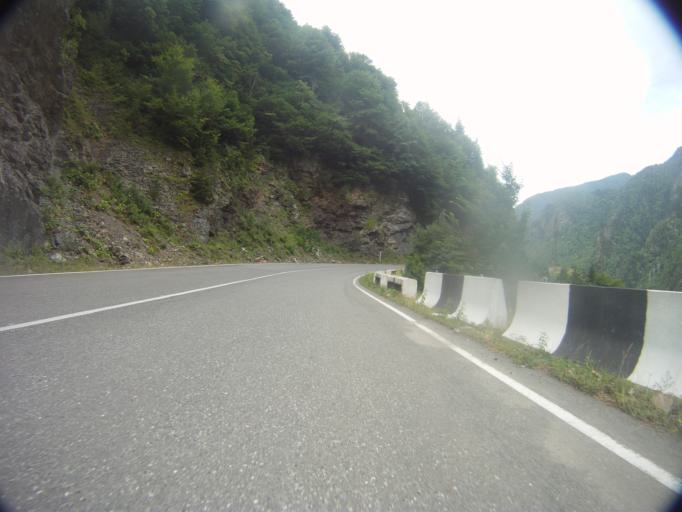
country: GE
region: Samegrelo and Zemo Svaneti
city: Jvari
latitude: 42.9013
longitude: 42.0541
